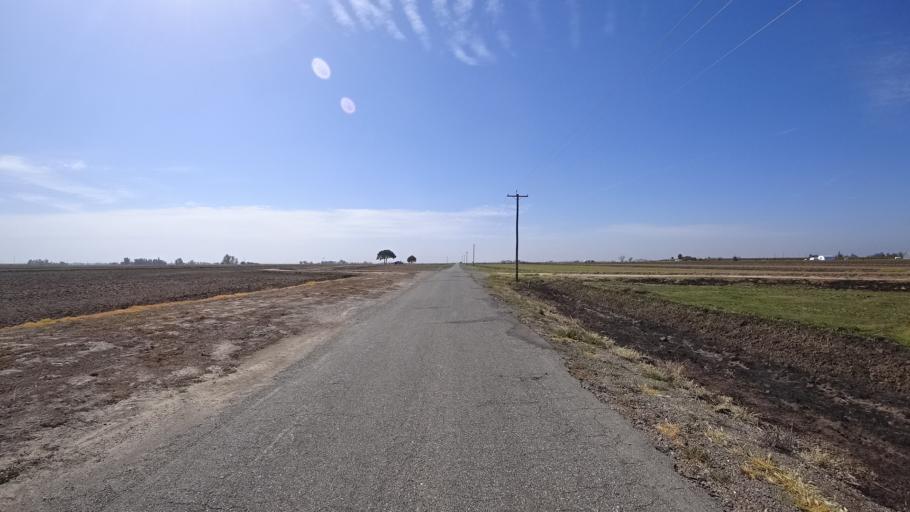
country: US
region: California
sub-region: Glenn County
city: Willows
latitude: 39.6062
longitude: -122.0744
